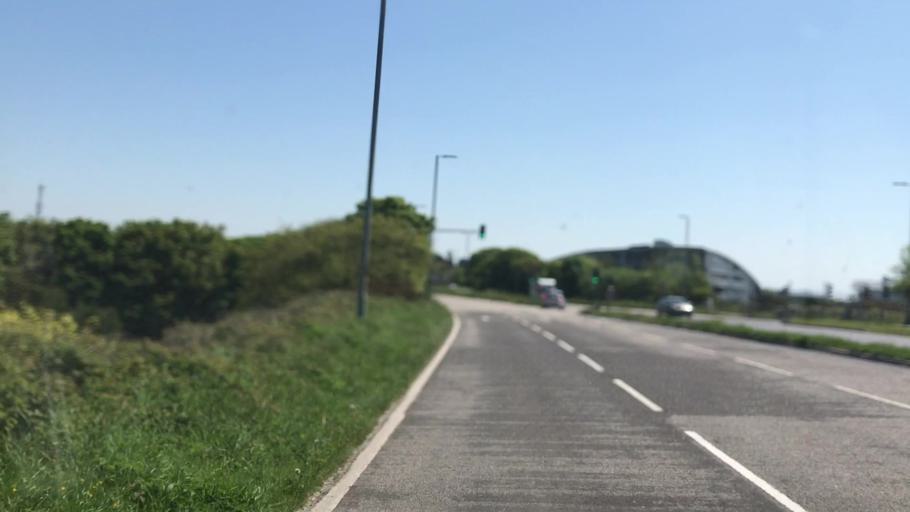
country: GB
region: England
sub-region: Cornwall
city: Truro
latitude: 50.2637
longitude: -5.1066
